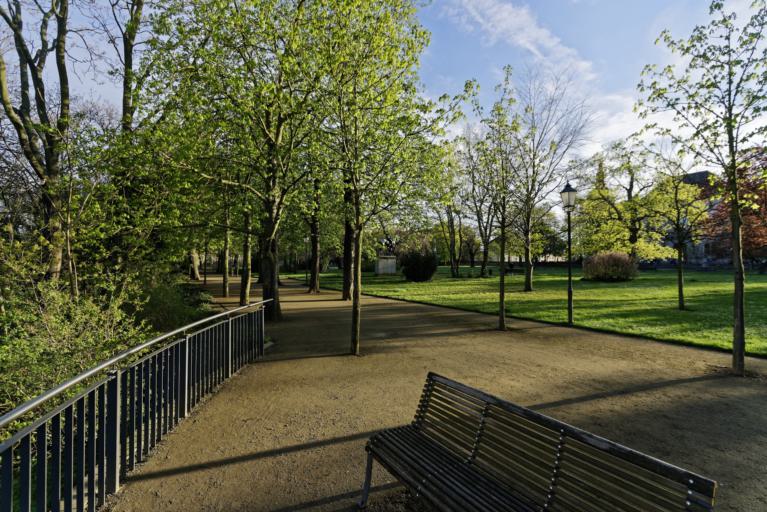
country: DE
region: Saxony-Anhalt
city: Merseburg
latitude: 51.3606
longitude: 12.0014
